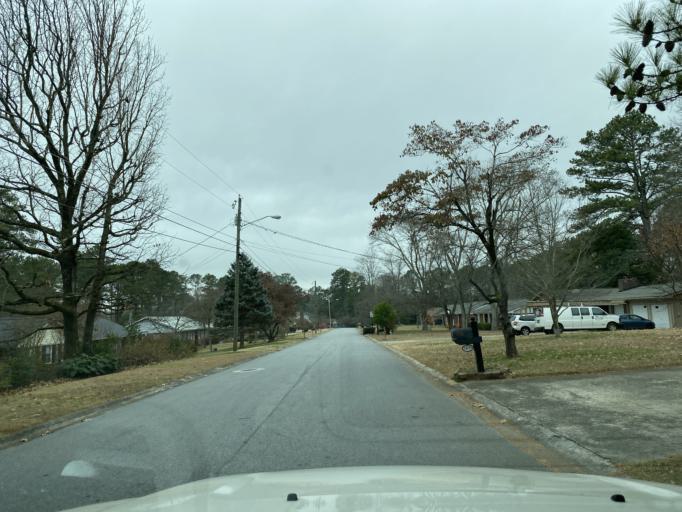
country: US
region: Georgia
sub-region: Cobb County
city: Fair Oaks
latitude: 33.9155
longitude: -84.5848
